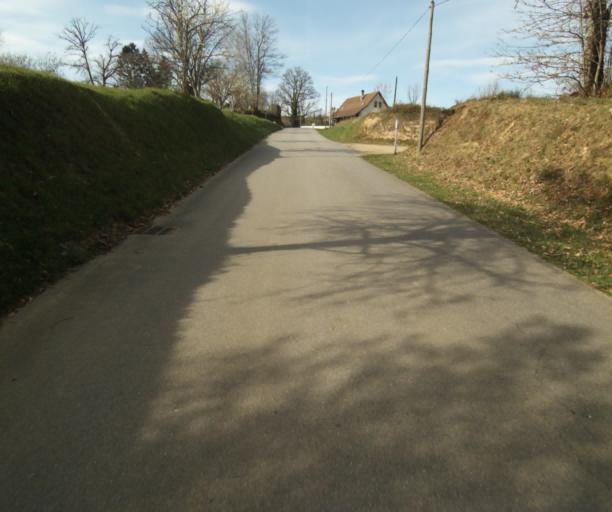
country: FR
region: Limousin
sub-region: Departement de la Correze
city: Naves
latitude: 45.3187
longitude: 1.7261
